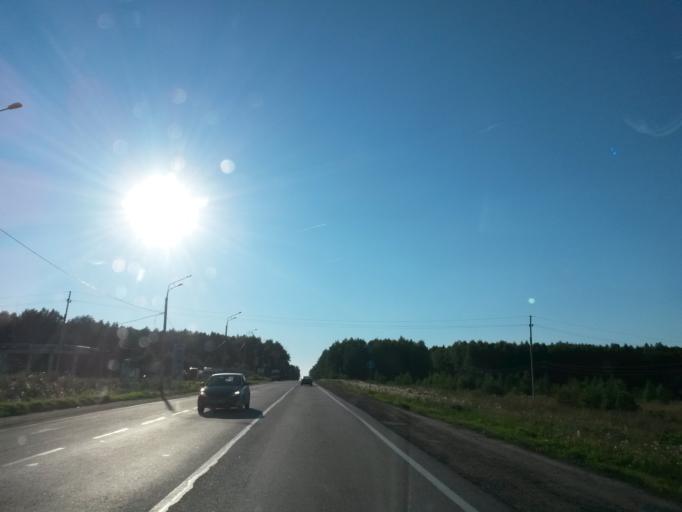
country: RU
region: Jaroslavl
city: Gavrilov-Yam
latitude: 57.2704
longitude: 39.9608
